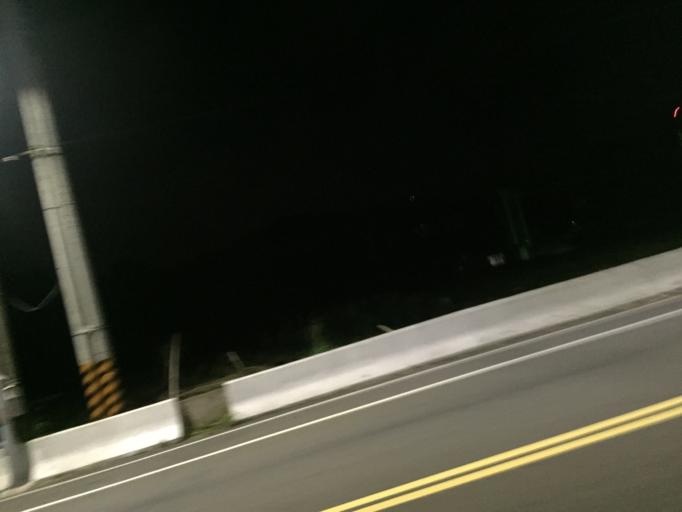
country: TW
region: Taiwan
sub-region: Hsinchu
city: Hsinchu
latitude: 24.7589
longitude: 120.9765
